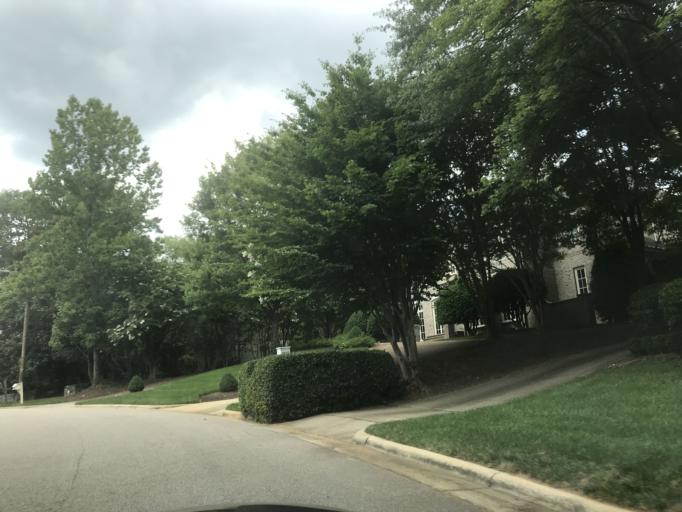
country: US
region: North Carolina
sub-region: Wake County
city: West Raleigh
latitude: 35.8323
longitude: -78.6491
